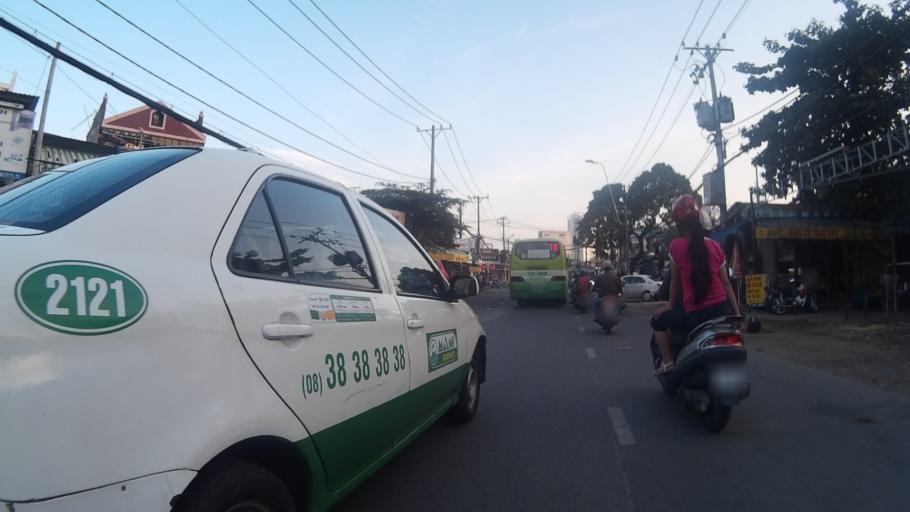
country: VN
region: Ho Chi Minh City
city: Quan Binh Thanh
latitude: 10.8106
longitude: 106.7115
